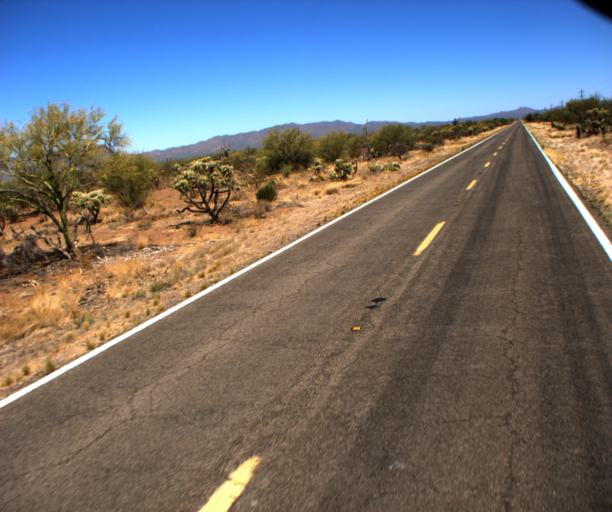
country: US
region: Arizona
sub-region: Pima County
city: Sells
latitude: 32.0382
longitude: -112.0158
